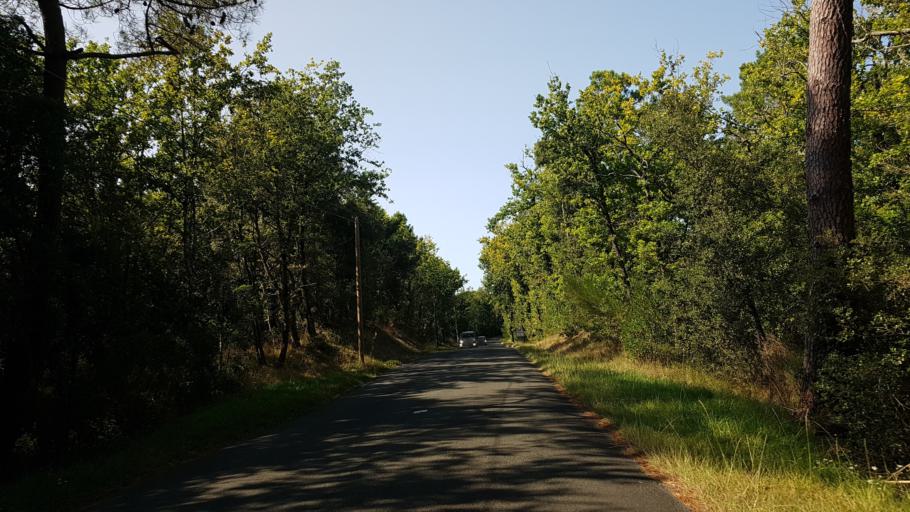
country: FR
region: Poitou-Charentes
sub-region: Departement de la Charente-Maritime
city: Saint-Palais-sur-Mer
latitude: 45.6628
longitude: -1.1188
